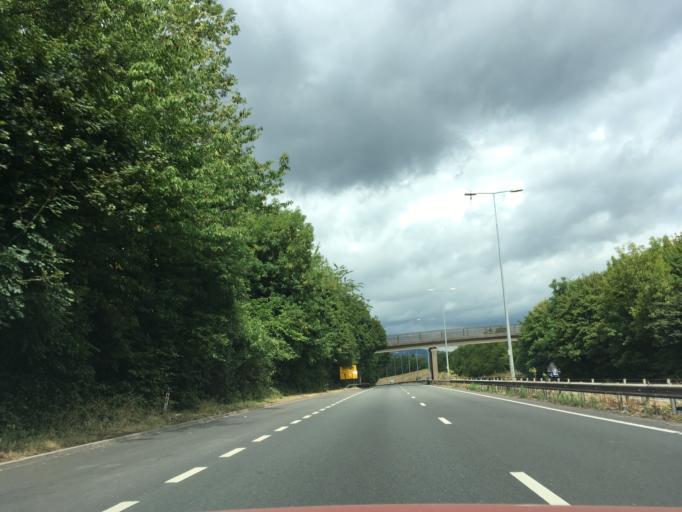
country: GB
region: Wales
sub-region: Torfaen County Borough
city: New Inn
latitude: 51.6718
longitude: -3.0076
